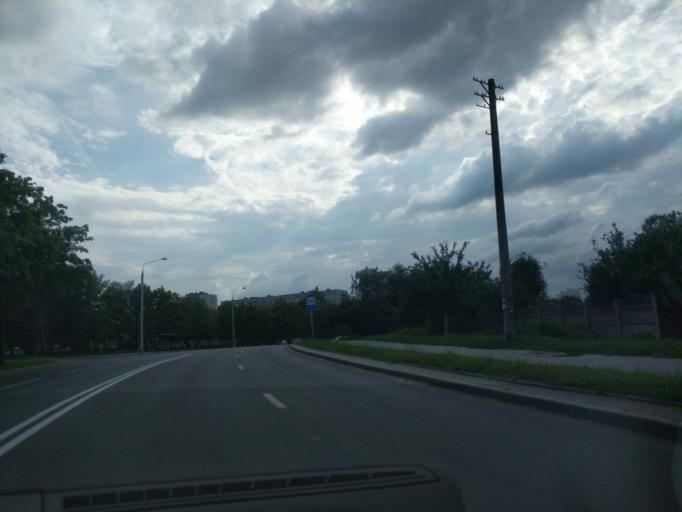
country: BY
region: Minsk
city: Malinovka
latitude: 53.8524
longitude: 27.4653
